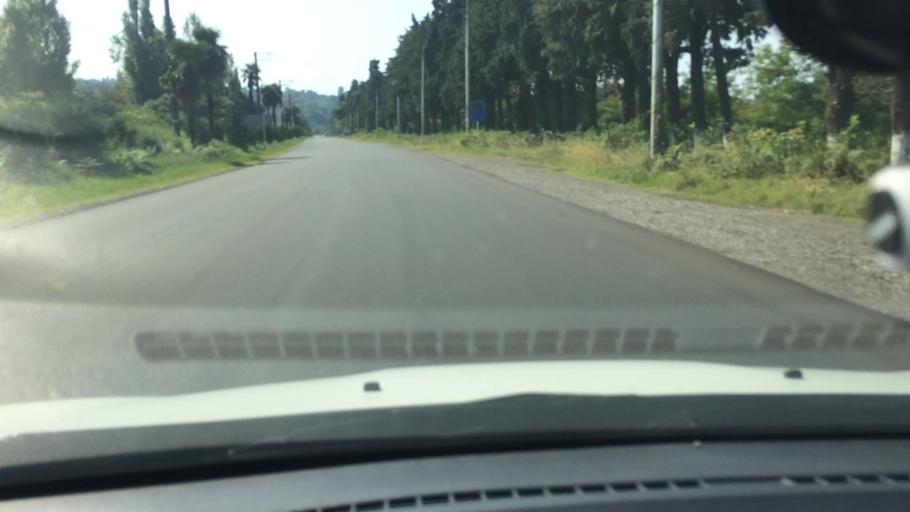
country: GE
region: Ajaria
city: Kobuleti
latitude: 41.7893
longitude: 41.7674
